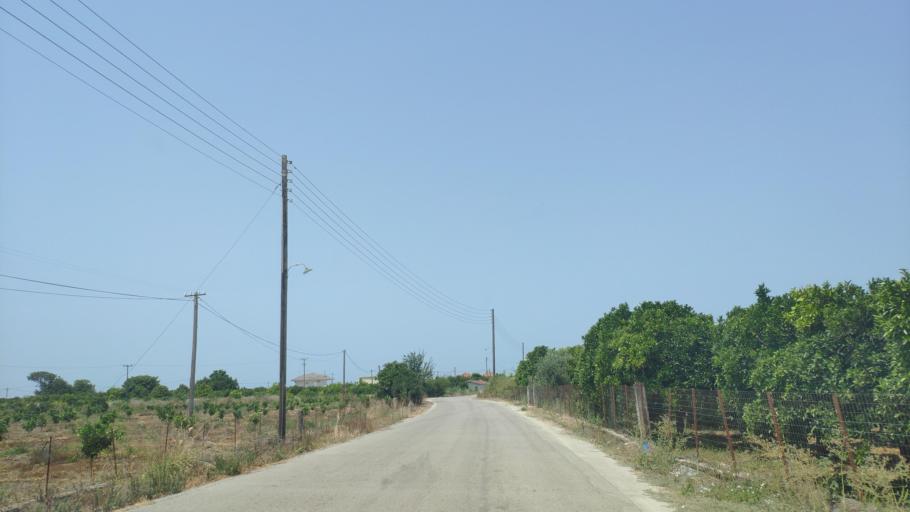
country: GR
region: Epirus
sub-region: Nomos Artas
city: Neochori
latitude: 39.0617
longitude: 21.0595
